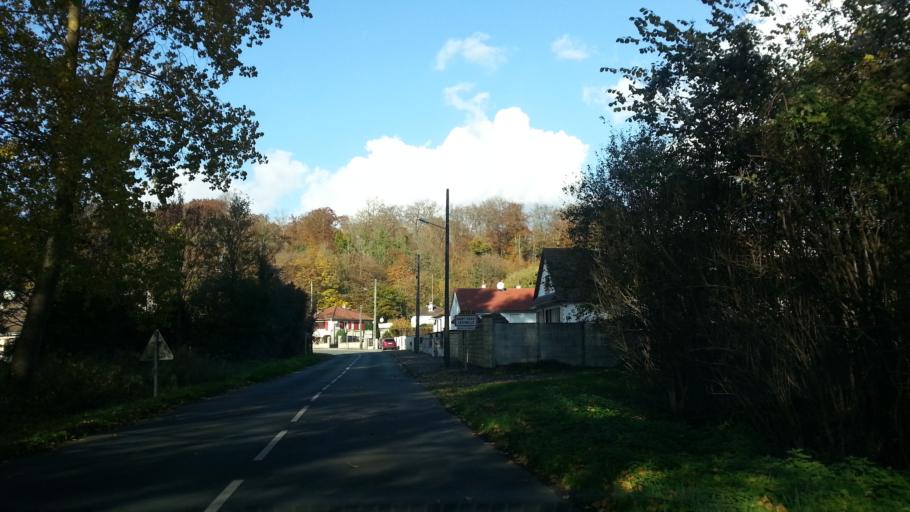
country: FR
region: Picardie
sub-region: Departement de l'Oise
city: Cires-les-Mello
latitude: 49.2658
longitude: 2.3720
